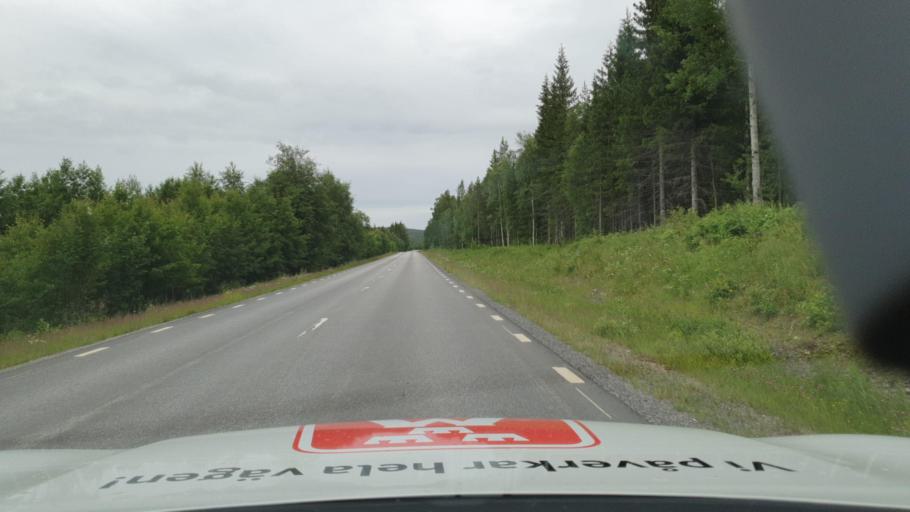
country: SE
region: Vaesterbotten
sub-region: Nordmalings Kommun
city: Nordmaling
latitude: 63.6993
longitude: 19.3665
